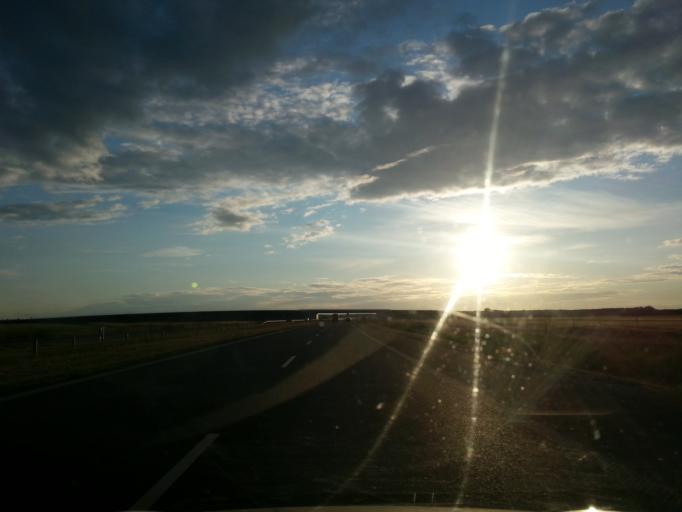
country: PL
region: Lodz Voivodeship
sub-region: Powiat wieruszowski
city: Sokolniki
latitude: 51.3191
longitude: 18.3542
